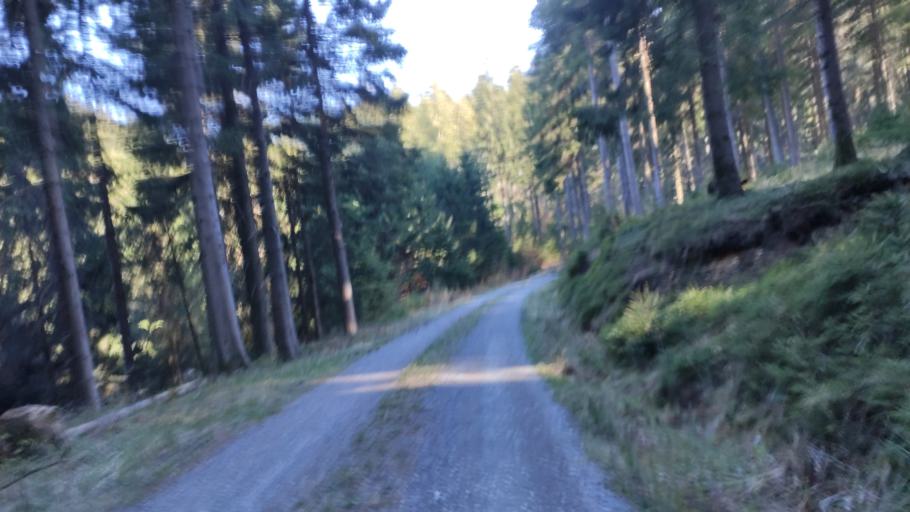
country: DE
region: Bavaria
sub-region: Upper Franconia
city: Reichenbach
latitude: 50.4440
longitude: 11.4368
